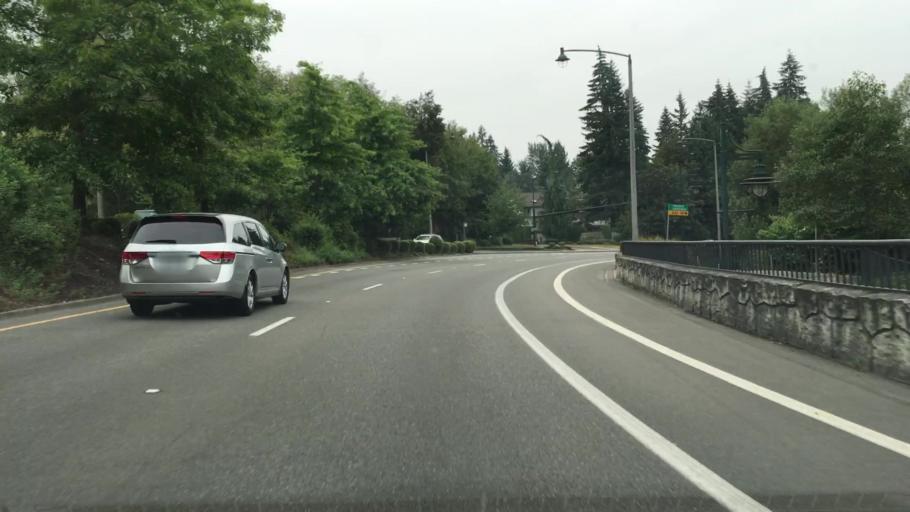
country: US
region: Washington
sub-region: King County
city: Newcastle
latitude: 47.5299
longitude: -122.1627
